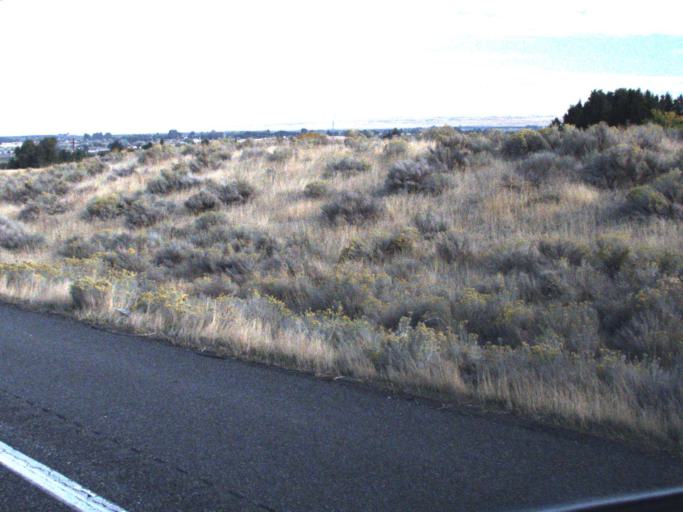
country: US
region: Washington
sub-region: Benton County
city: Prosser
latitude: 46.2121
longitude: -119.7394
